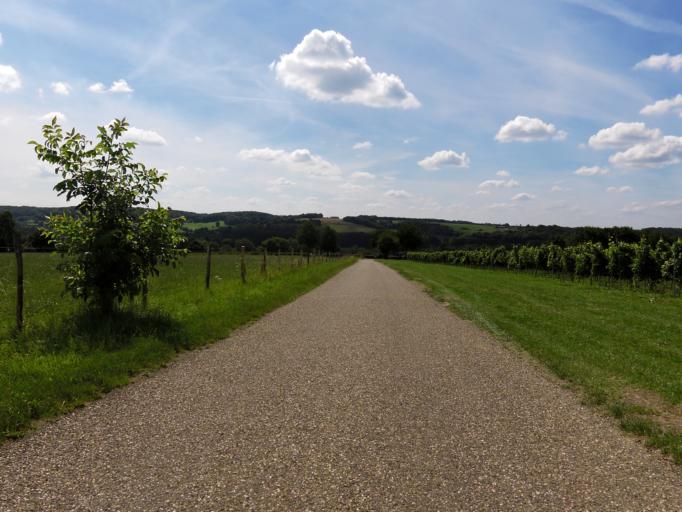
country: NL
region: Limburg
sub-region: Valkenburg aan de Geul
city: Schin op Geul
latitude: 50.8459
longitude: 5.8961
